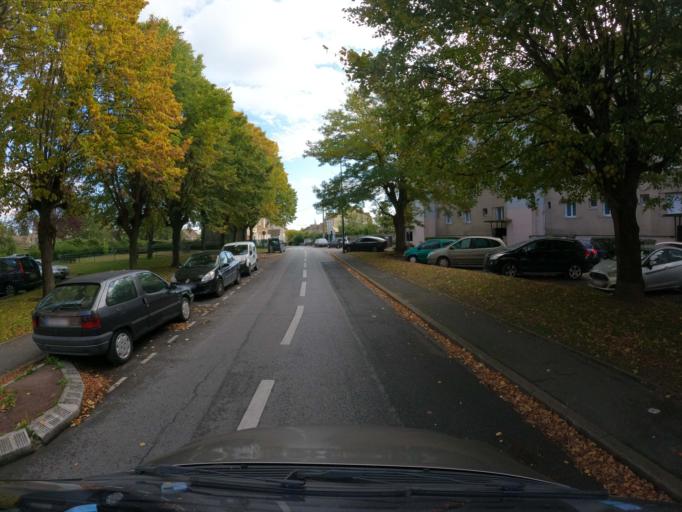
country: FR
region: Ile-de-France
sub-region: Departement de Seine-et-Marne
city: Brou-sur-Chantereine
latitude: 48.8815
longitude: 2.6205
